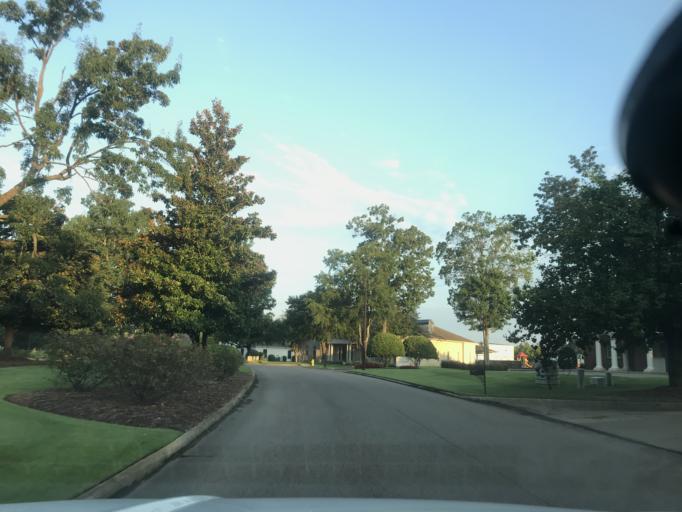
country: US
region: Alabama
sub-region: Montgomery County
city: Pike Road
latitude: 32.3683
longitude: -86.1678
